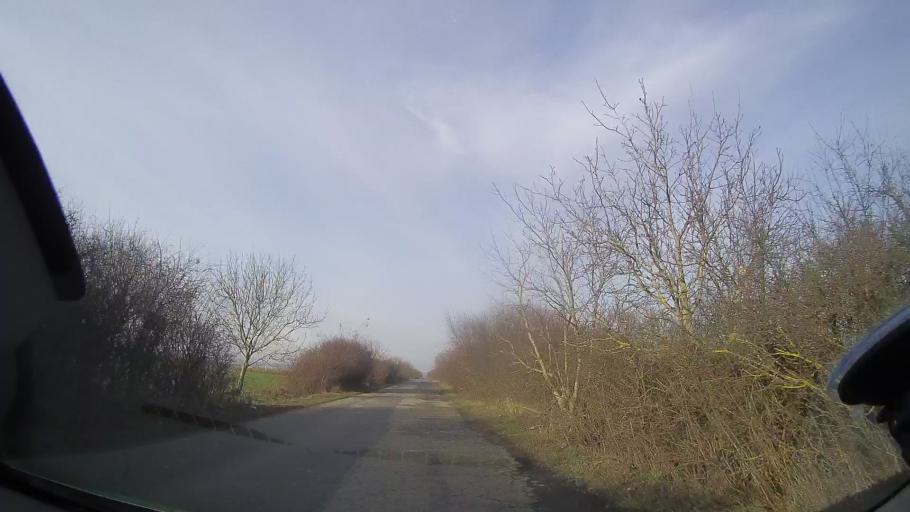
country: RO
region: Bihor
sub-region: Comuna Spinus
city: Spinus
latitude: 47.2149
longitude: 22.1762
